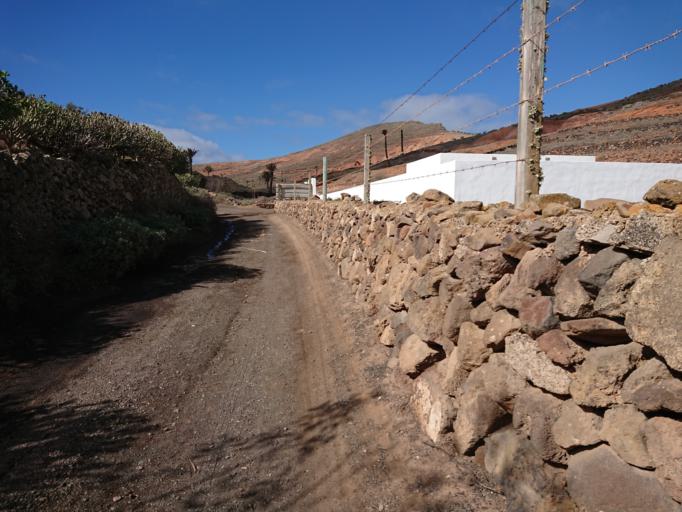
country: ES
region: Canary Islands
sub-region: Provincia de Las Palmas
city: Haria
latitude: 29.1448
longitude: -13.5110
